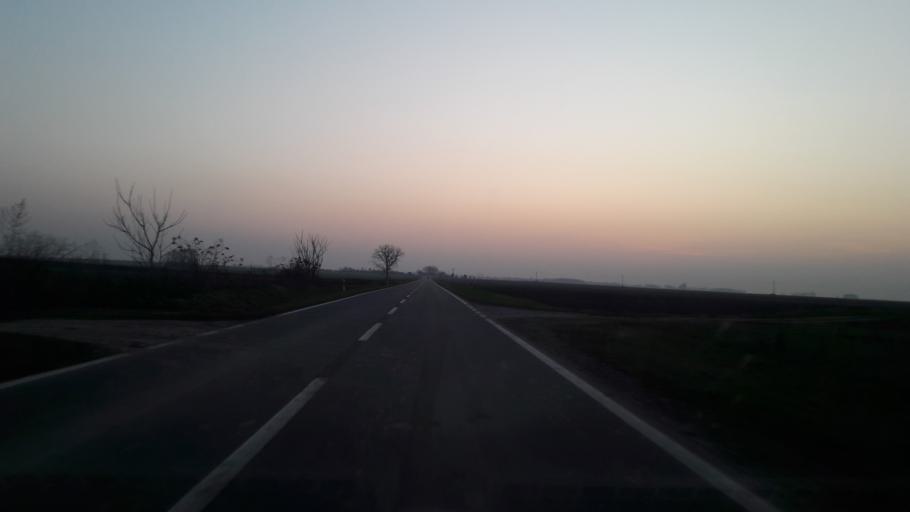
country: HR
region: Vukovarsko-Srijemska
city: Negoslavci
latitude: 45.2681
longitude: 18.9942
